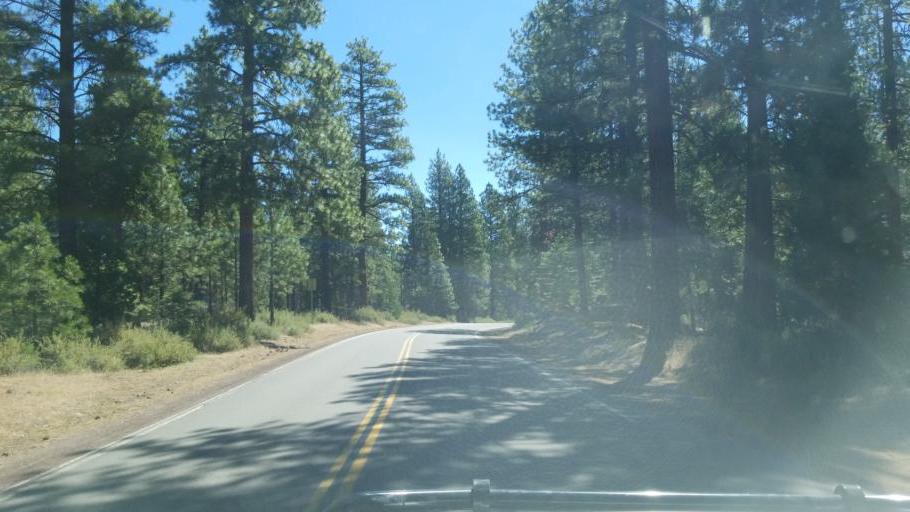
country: US
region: California
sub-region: Lassen County
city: Susanville
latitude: 40.4352
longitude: -120.7394
